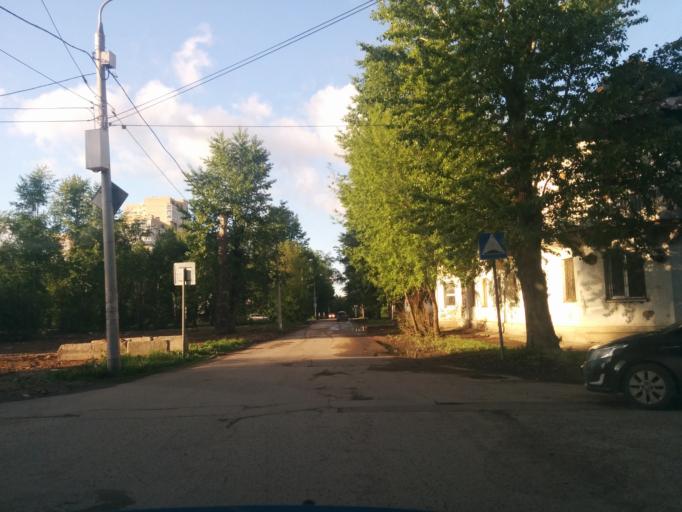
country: RU
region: Perm
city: Perm
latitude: 57.9982
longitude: 56.1807
